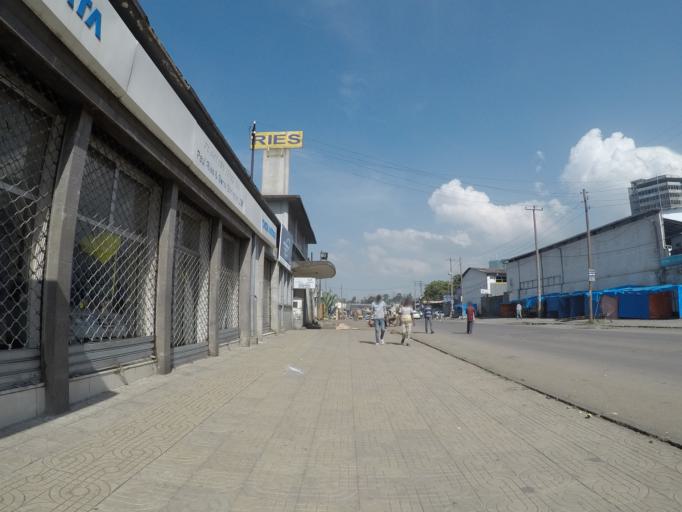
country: ET
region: Adis Abeba
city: Addis Ababa
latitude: 9.0325
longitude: 38.7464
